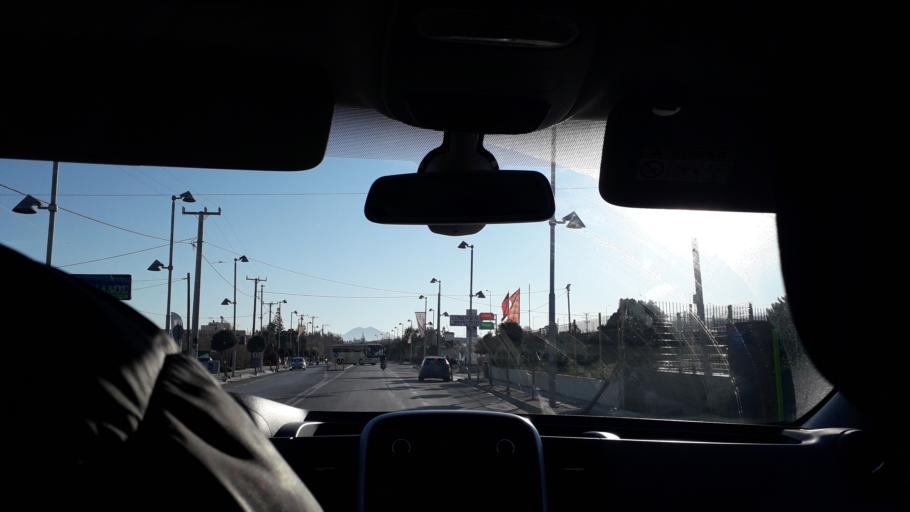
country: GR
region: Crete
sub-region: Nomos Rethymnis
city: Rethymno
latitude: 35.3660
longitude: 24.5141
